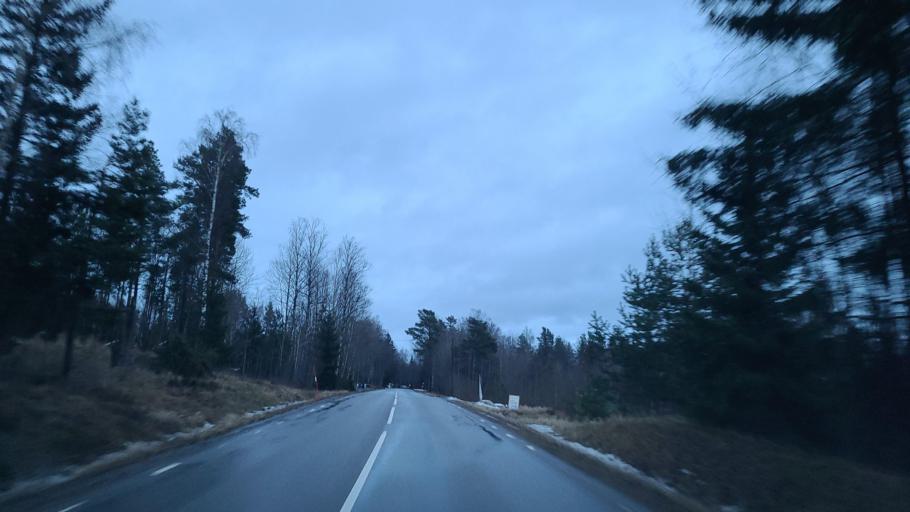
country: SE
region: Stockholm
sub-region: Norrtalje Kommun
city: Norrtalje
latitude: 59.7317
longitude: 18.5791
